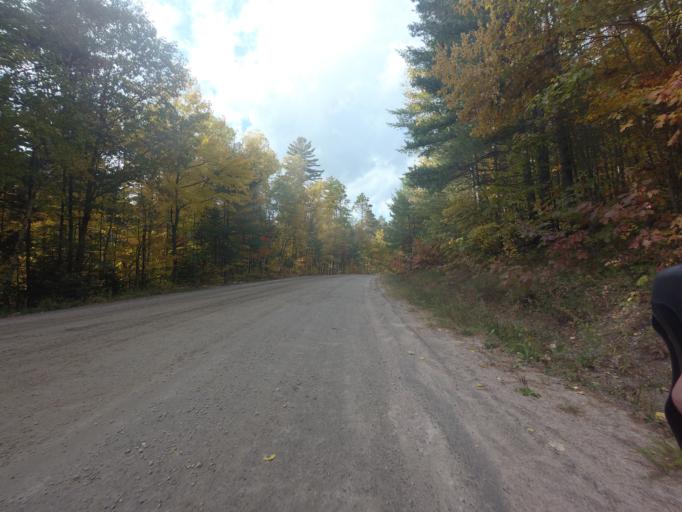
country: CA
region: Ontario
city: Petawawa
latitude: 45.8430
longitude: -77.5246
